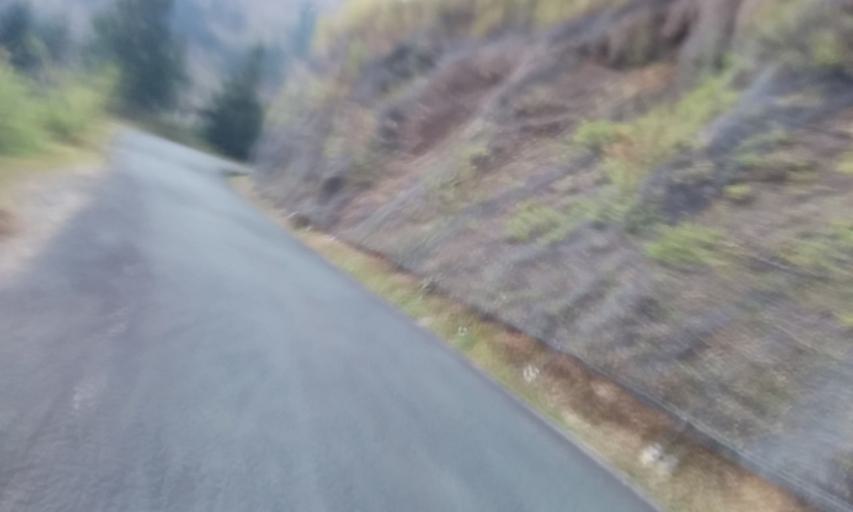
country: JP
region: Ehime
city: Saijo
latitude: 33.7901
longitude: 133.2784
